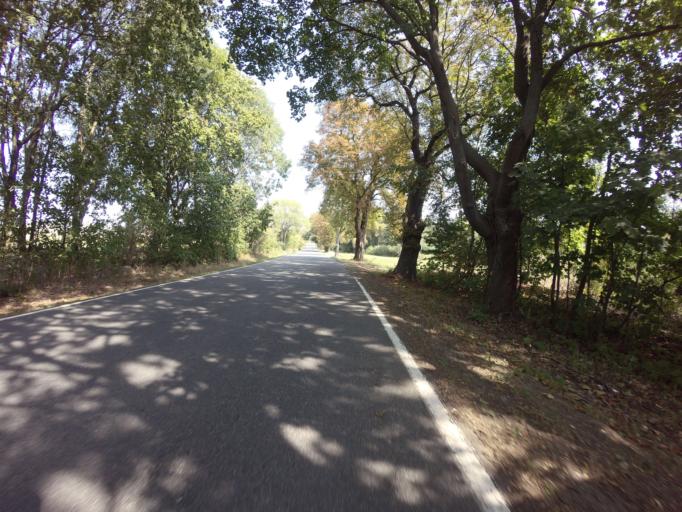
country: CZ
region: Central Bohemia
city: Petrovice
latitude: 49.6018
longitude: 14.3838
